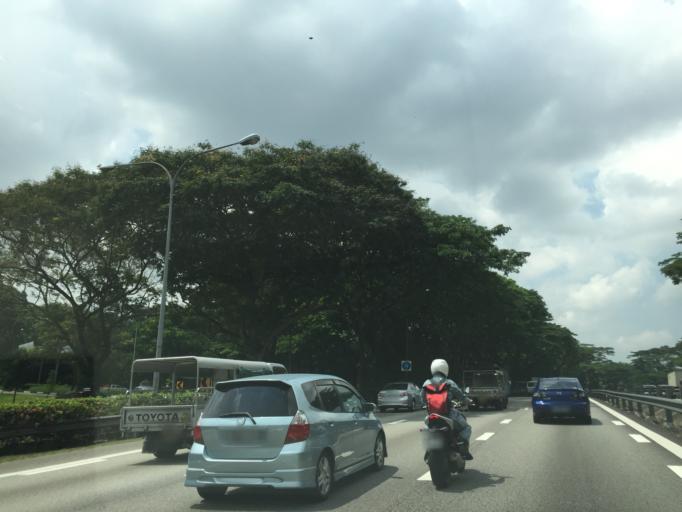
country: SG
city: Singapore
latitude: 1.3267
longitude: 103.8277
